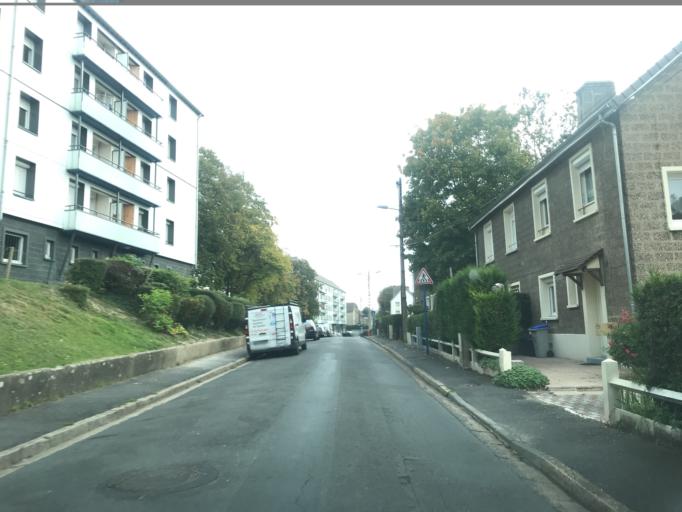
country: FR
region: Haute-Normandie
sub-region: Departement de la Seine-Maritime
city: Deville-les-Rouen
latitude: 49.4630
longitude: 1.0560
